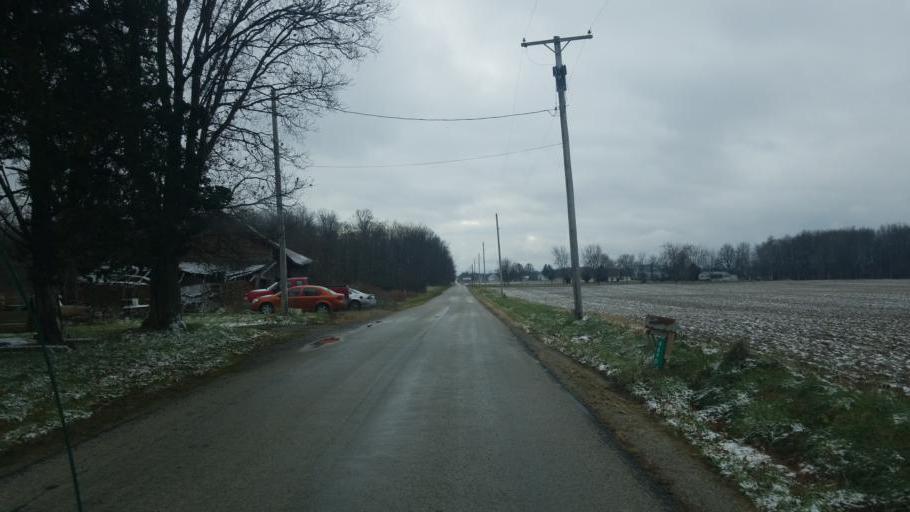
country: US
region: Ohio
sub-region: Richland County
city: Shelby
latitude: 40.8833
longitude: -82.5521
